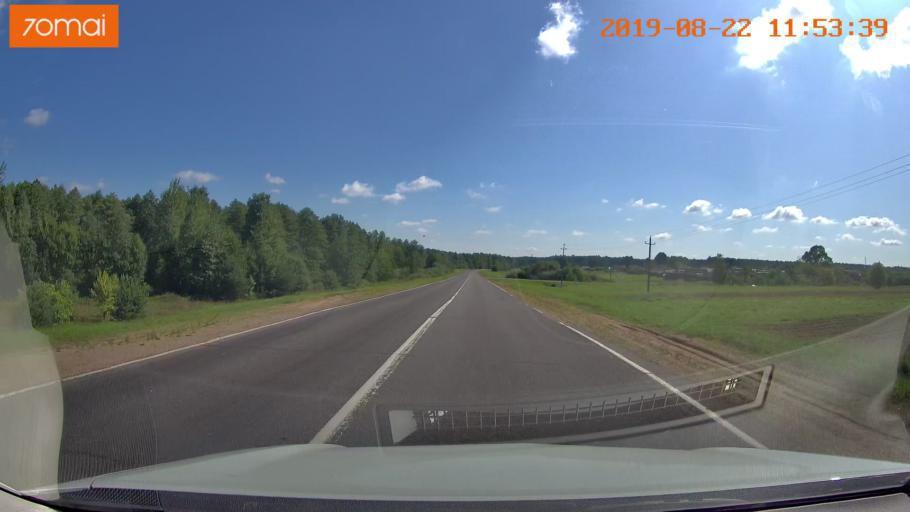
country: BY
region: Minsk
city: Uzda
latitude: 53.4369
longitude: 27.5071
